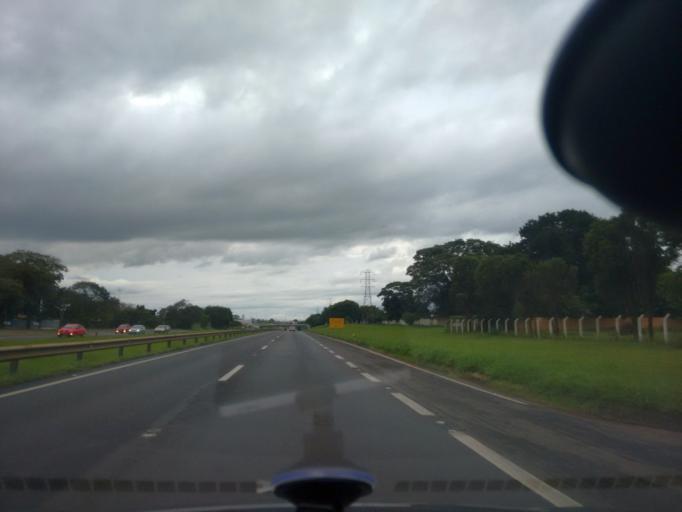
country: BR
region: Sao Paulo
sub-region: Rio Claro
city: Rio Claro
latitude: -22.4307
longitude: -47.5719
